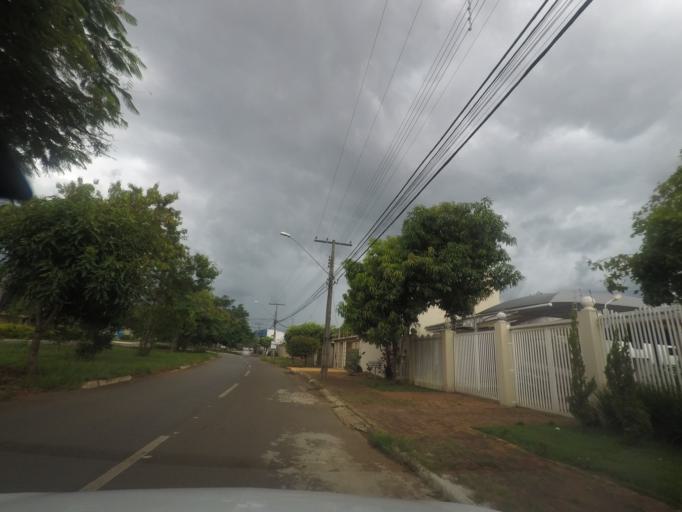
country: BR
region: Goias
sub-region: Goiania
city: Goiania
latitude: -16.6411
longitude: -49.2254
